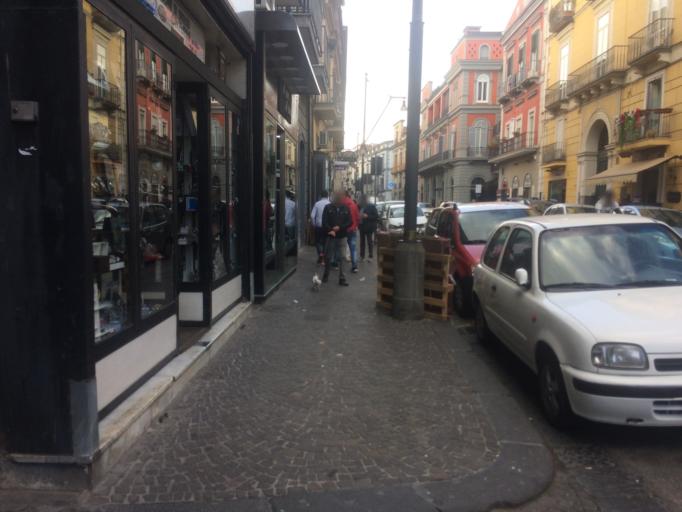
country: IT
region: Campania
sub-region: Provincia di Napoli
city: Frattamaggiore
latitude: 40.9410
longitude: 14.2706
